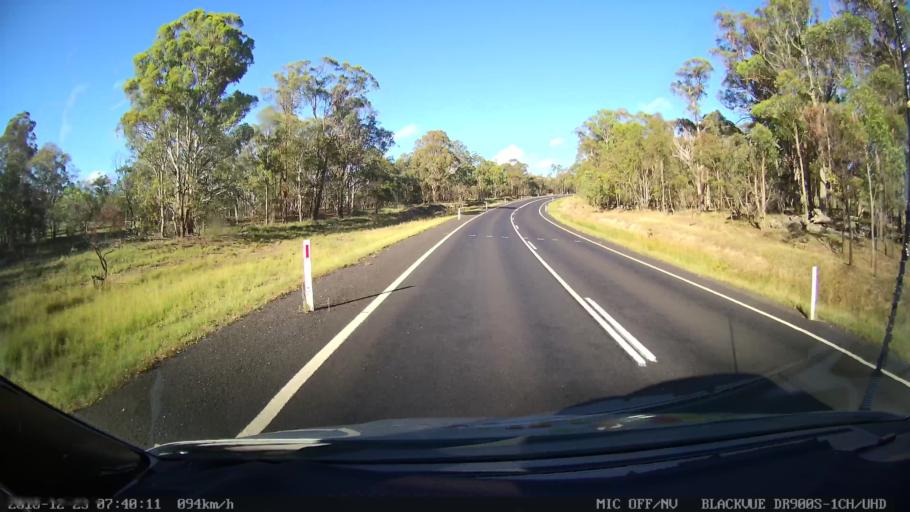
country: AU
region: New South Wales
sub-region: Armidale Dumaresq
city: Enmore
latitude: -30.5141
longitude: 152.0110
